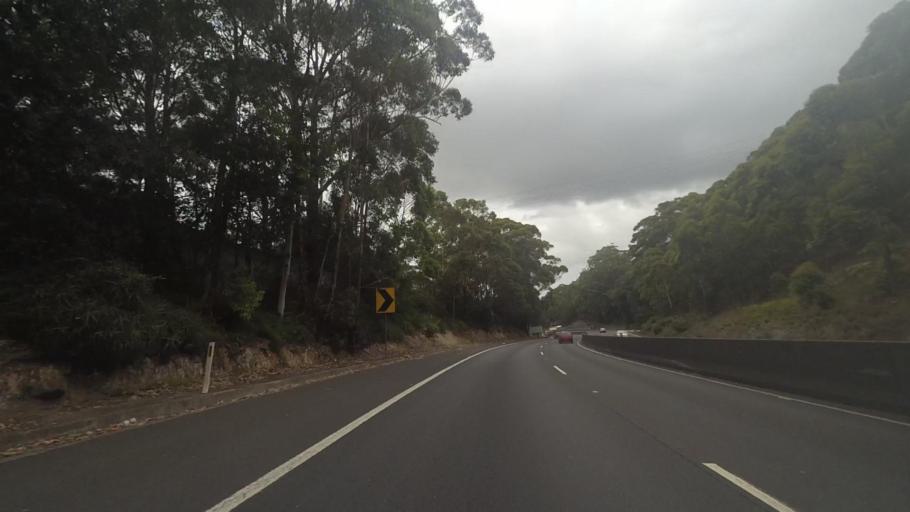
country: AU
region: New South Wales
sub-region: Wollongong
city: Mount Ousley
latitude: -34.3980
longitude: 150.8685
